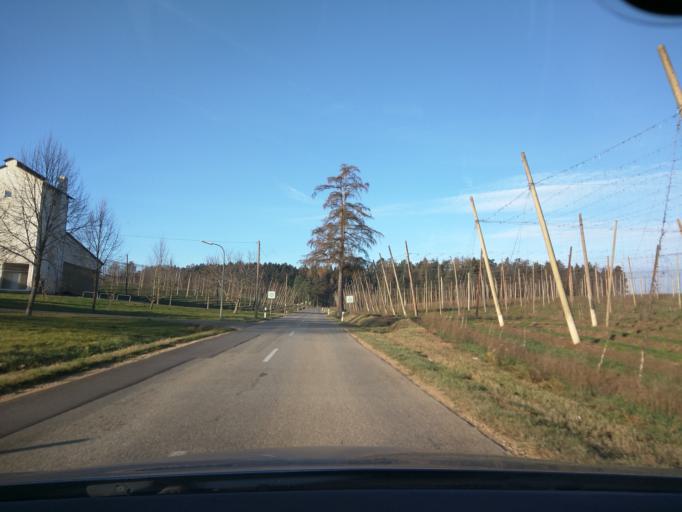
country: DE
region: Bavaria
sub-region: Upper Bavaria
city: Wolnzach
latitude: 48.5837
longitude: 11.6636
